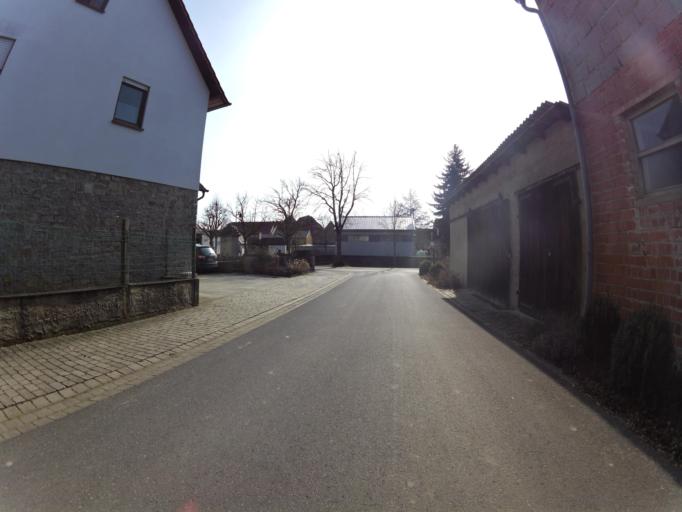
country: DE
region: Bavaria
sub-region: Regierungsbezirk Unterfranken
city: Prosselsheim
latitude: 49.8250
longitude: 10.1242
